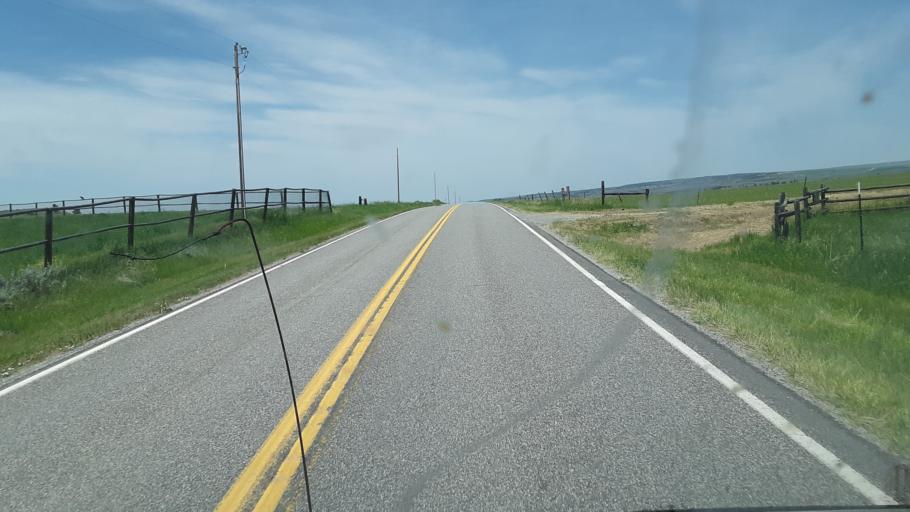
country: US
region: Montana
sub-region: Stillwater County
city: Columbus
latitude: 45.5841
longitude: -109.1879
